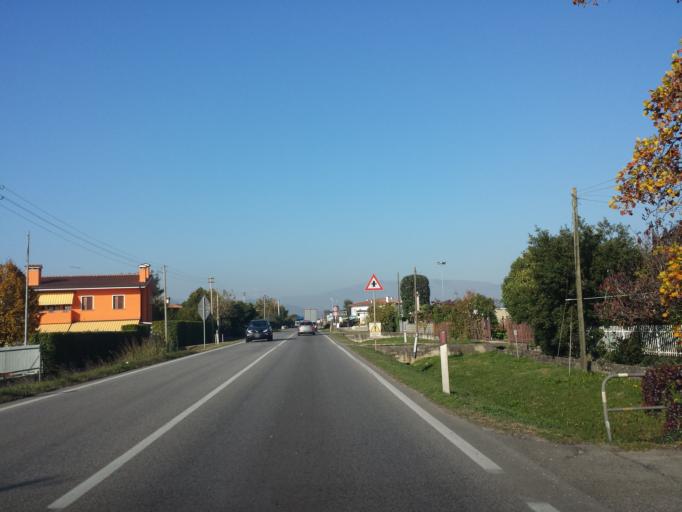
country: IT
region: Veneto
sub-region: Provincia di Treviso
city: Caerano di San Marco
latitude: 45.7646
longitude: 11.9948
